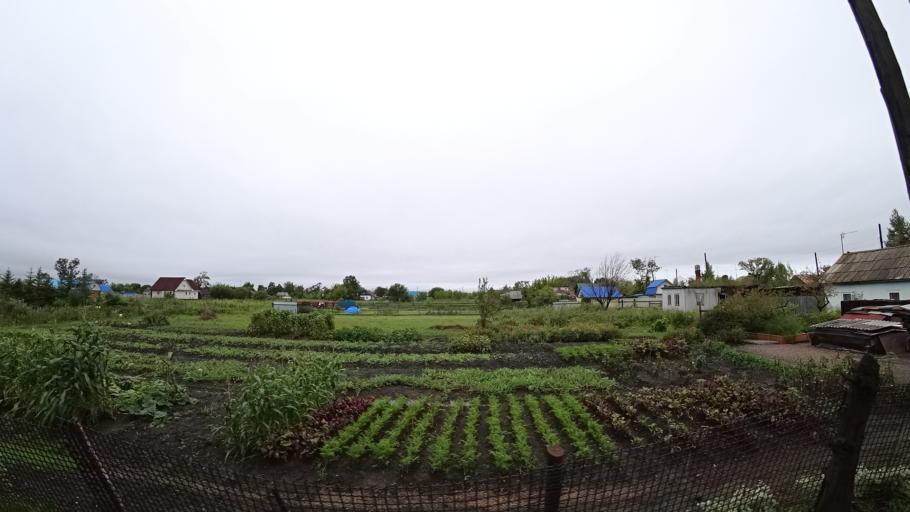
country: RU
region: Primorskiy
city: Monastyrishche
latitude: 44.2108
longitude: 132.4336
